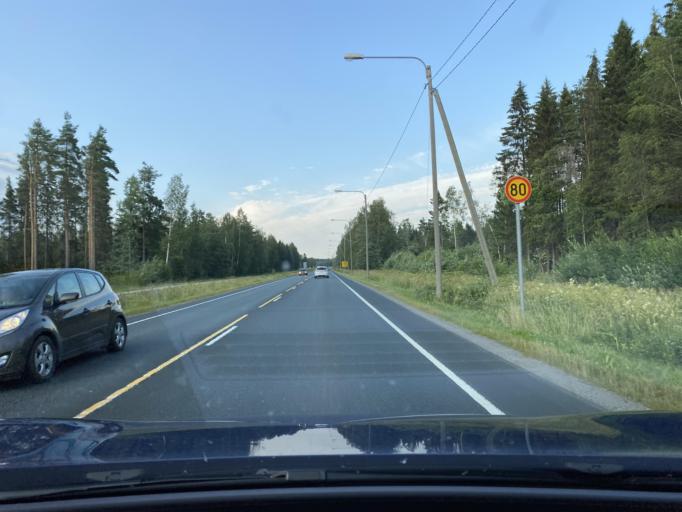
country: FI
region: Ostrobothnia
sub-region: Jakobstadsregionen
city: Bennaes
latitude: 63.6340
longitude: 22.8624
